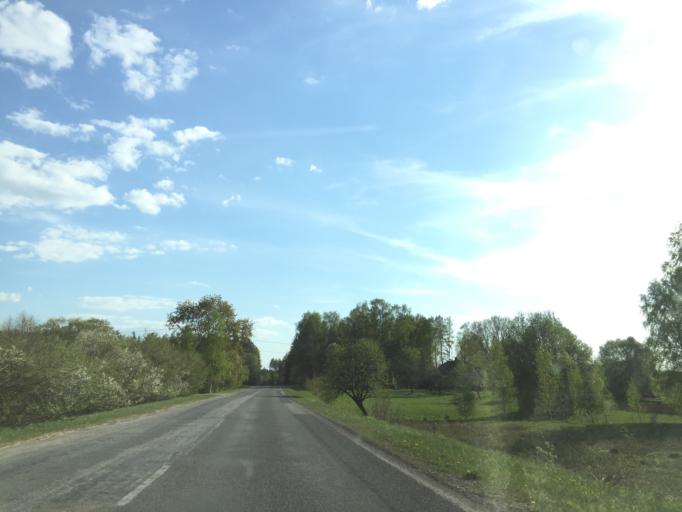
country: LV
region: Sigulda
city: Sigulda
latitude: 57.2496
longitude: 24.8712
